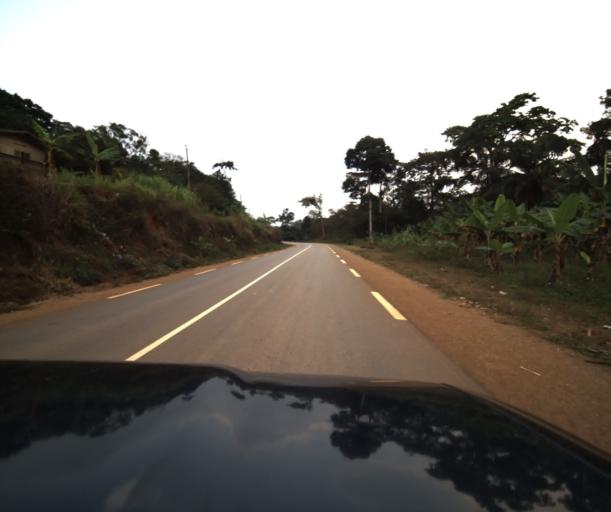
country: CM
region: Centre
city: Mbankomo
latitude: 3.7688
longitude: 11.4098
